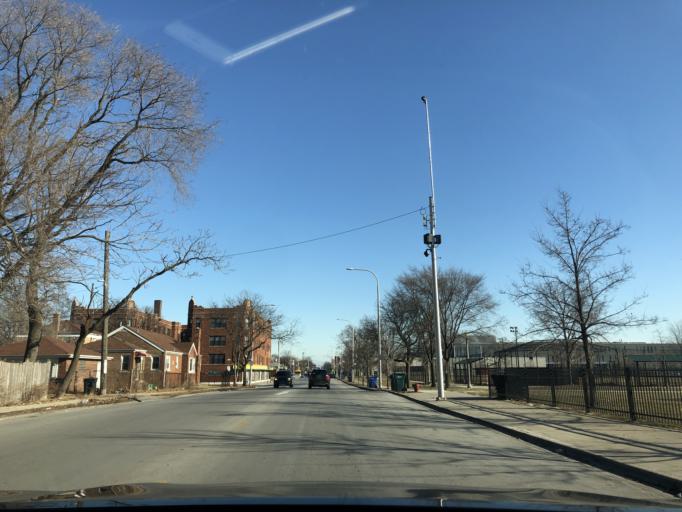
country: US
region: Illinois
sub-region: Cook County
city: Chicago
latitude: 41.7588
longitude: -87.5804
